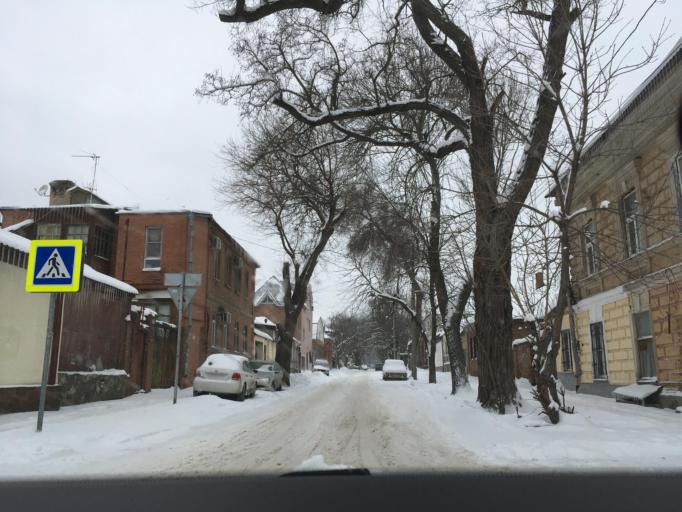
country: RU
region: Rostov
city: Rostov-na-Donu
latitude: 47.2308
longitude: 39.7539
